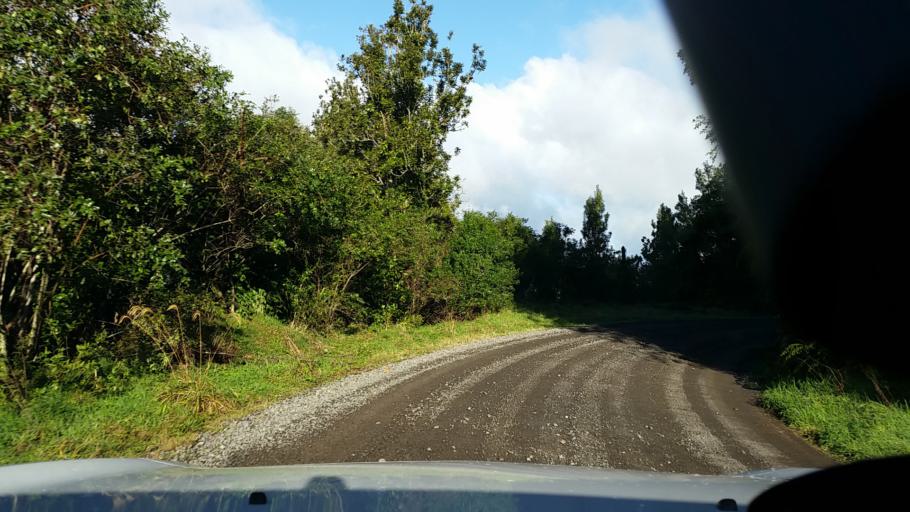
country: NZ
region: Bay of Plenty
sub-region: Kawerau District
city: Kawerau
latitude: -38.0246
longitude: 176.5661
